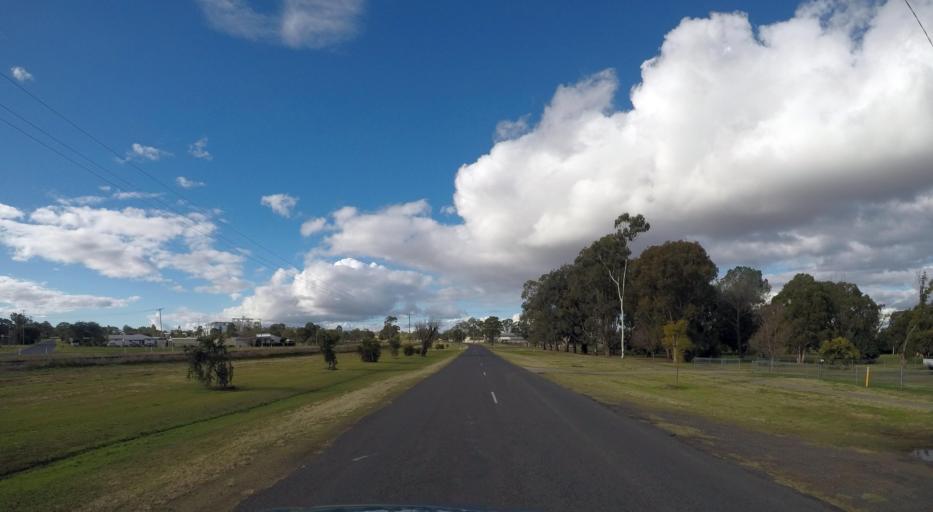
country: AU
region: Queensland
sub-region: Toowoomba
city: Westbrook
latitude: -27.7133
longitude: 151.6382
